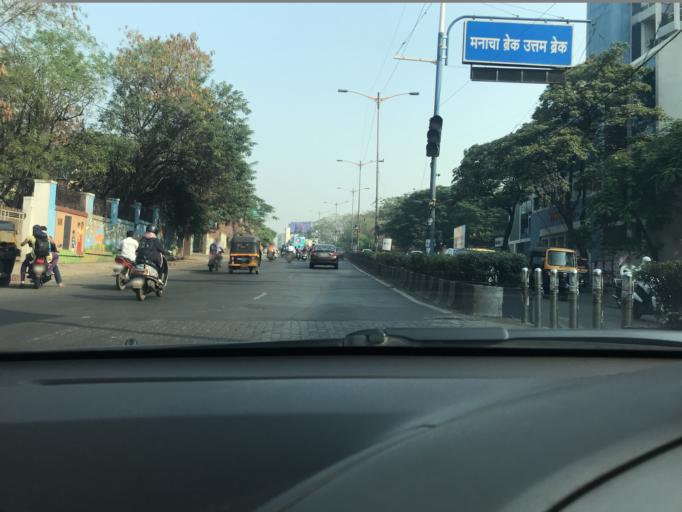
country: IN
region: Maharashtra
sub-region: Pune Division
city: Shivaji Nagar
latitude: 18.5220
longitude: 73.8293
